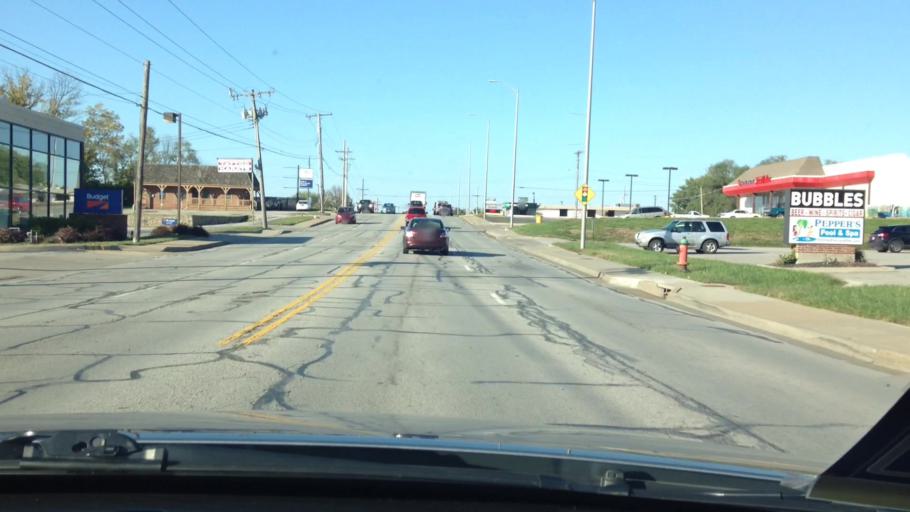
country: US
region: Missouri
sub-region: Clay County
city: Gladstone
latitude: 39.2295
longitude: -94.5761
